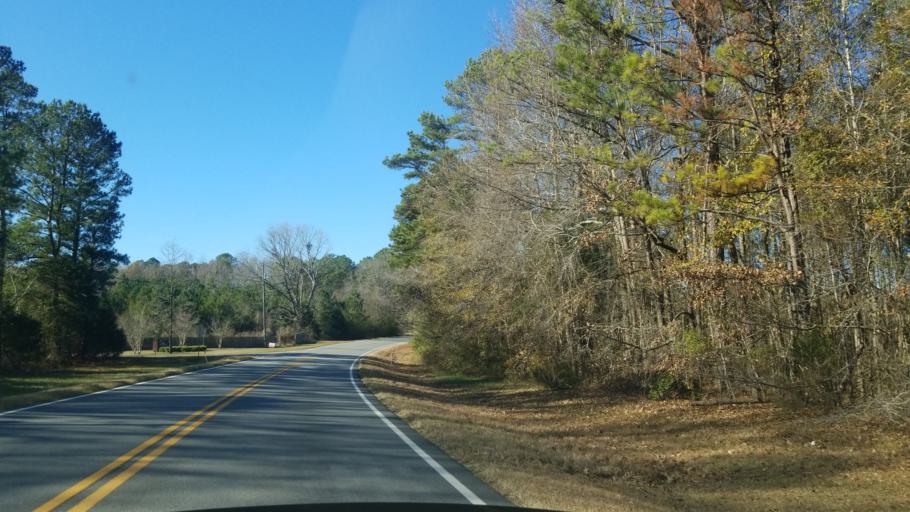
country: US
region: Georgia
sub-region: Harris County
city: Hamilton
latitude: 32.6704
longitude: -84.9032
